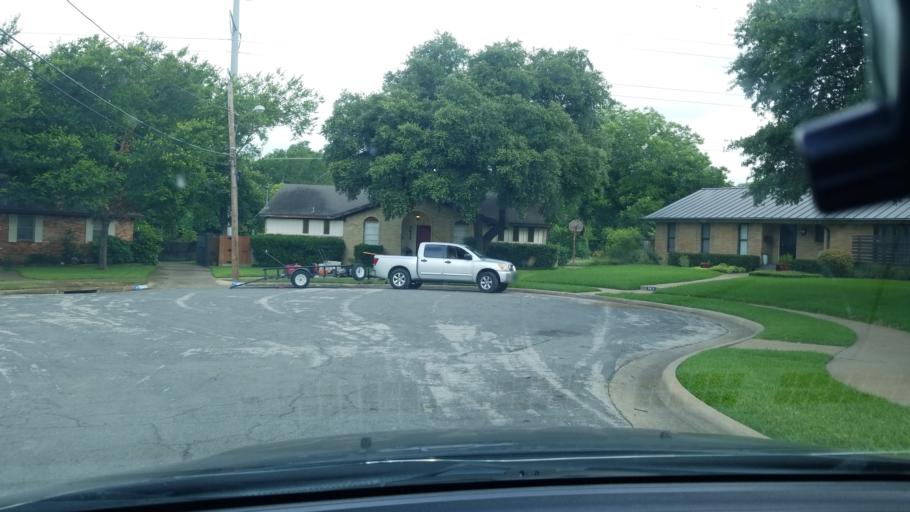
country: US
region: Texas
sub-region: Dallas County
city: Highland Park
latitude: 32.8219
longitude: -96.6959
